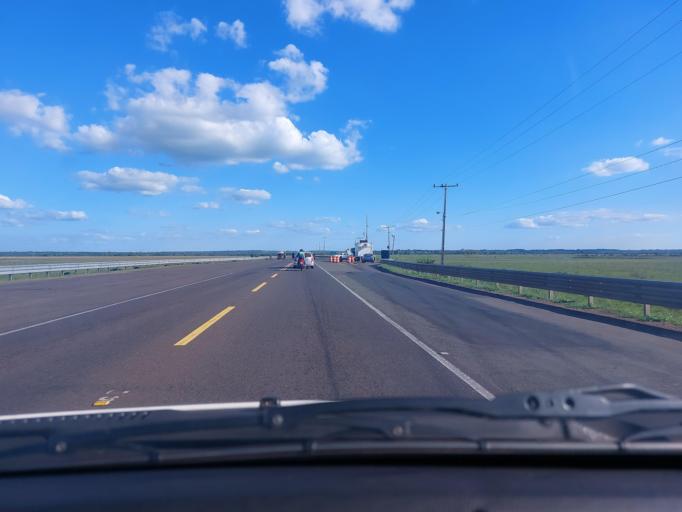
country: PY
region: Cordillera
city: Arroyos y Esteros
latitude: -25.0372
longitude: -57.0363
